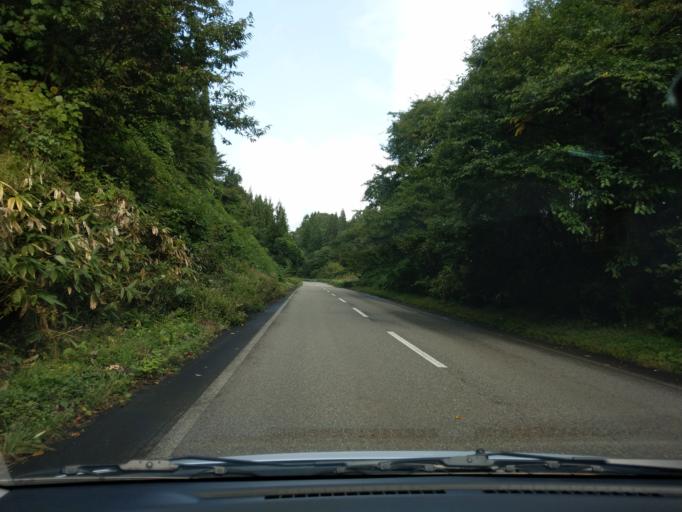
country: JP
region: Akita
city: Omagari
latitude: 39.4672
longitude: 140.3180
